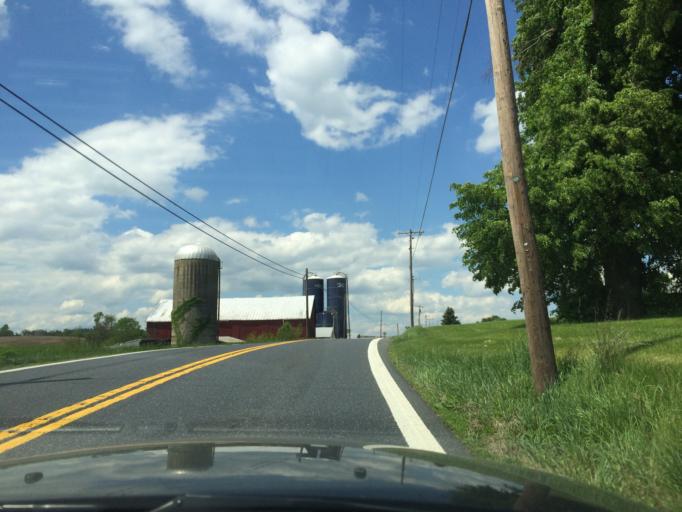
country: US
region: Maryland
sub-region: Frederick County
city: Linganore
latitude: 39.4904
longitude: -77.2423
